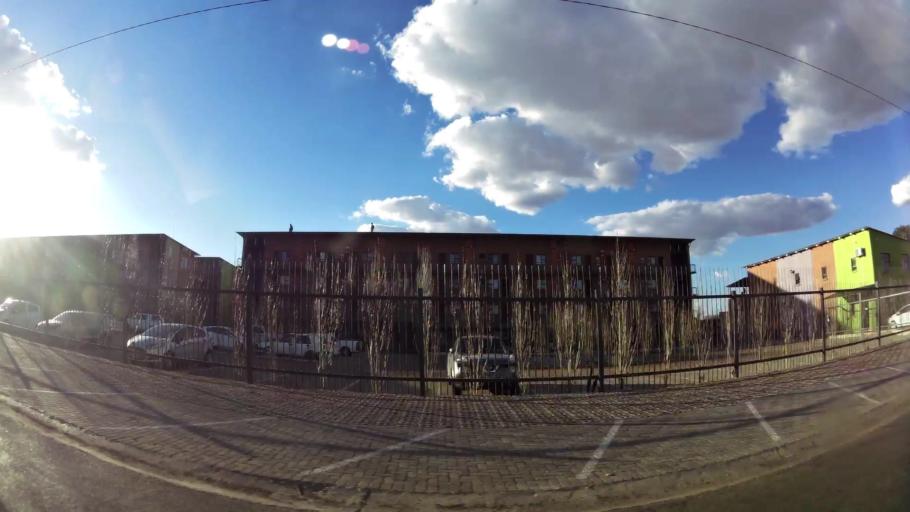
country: ZA
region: North-West
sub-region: Dr Kenneth Kaunda District Municipality
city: Potchefstroom
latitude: -26.7066
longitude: 27.0865
